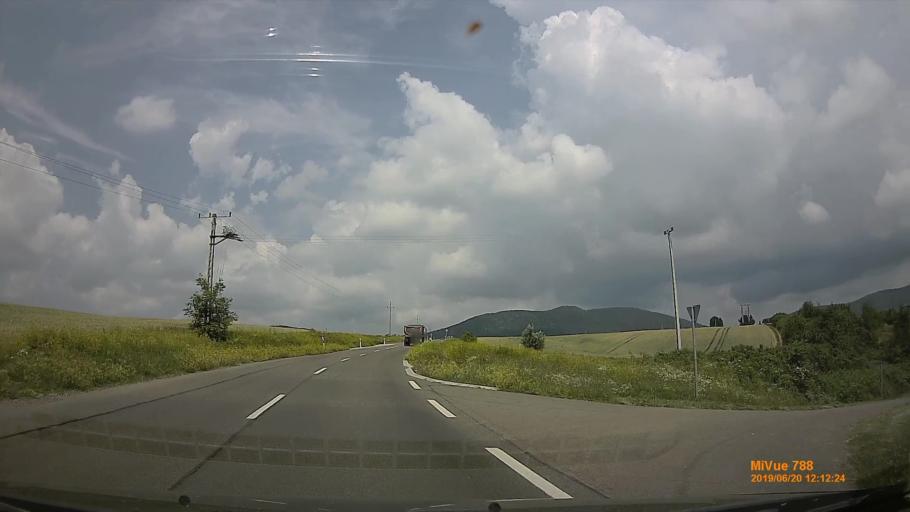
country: HU
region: Baranya
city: Hosszuheteny
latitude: 46.1466
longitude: 18.3467
